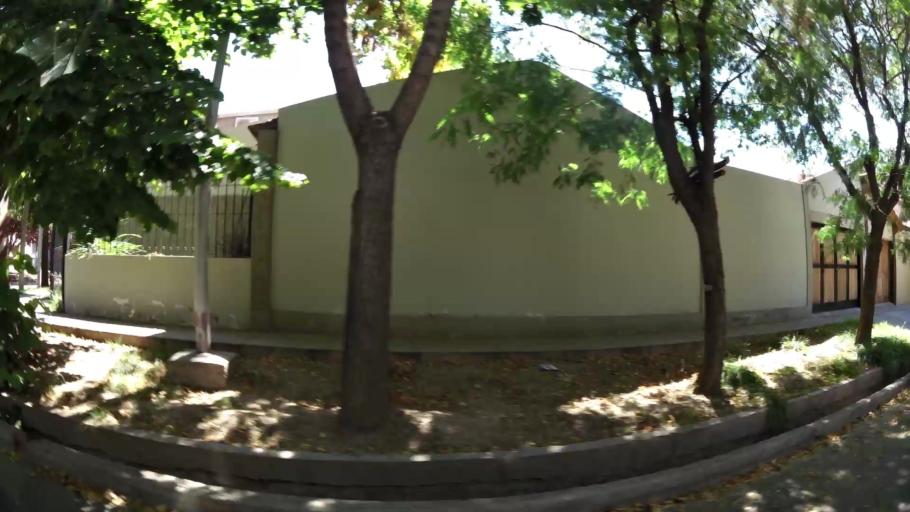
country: AR
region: Mendoza
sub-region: Departamento de Godoy Cruz
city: Godoy Cruz
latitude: -32.9773
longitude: -68.8554
